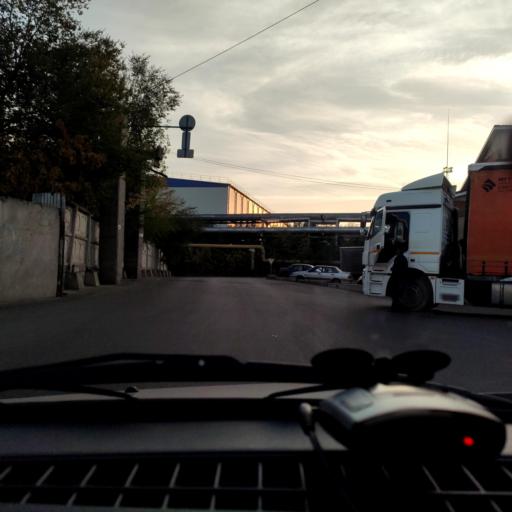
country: RU
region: Voronezj
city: Voronezh
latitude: 51.6875
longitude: 39.1537
